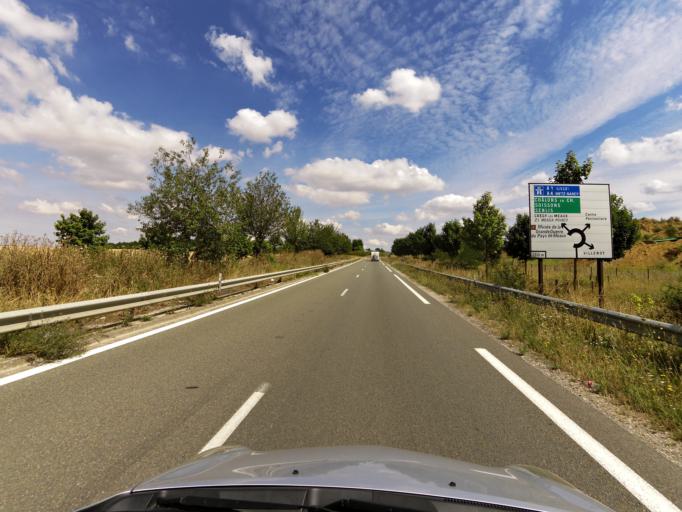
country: FR
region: Ile-de-France
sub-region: Departement de Seine-et-Marne
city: Chauconin-Neufmontiers
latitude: 48.9619
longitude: 2.8595
